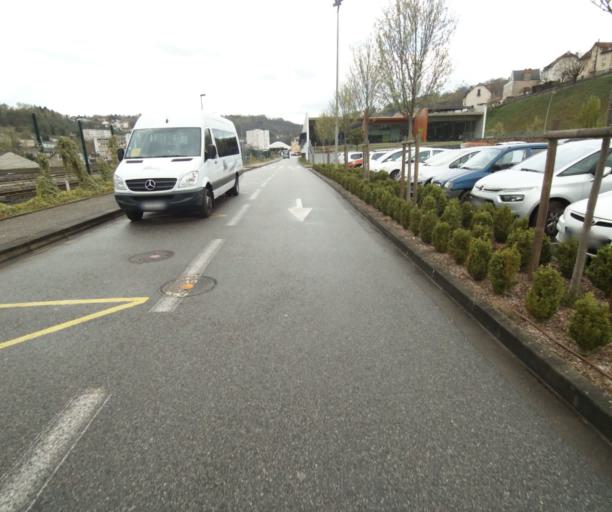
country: FR
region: Limousin
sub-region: Departement de la Correze
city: Tulle
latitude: 45.2571
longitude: 1.7595
